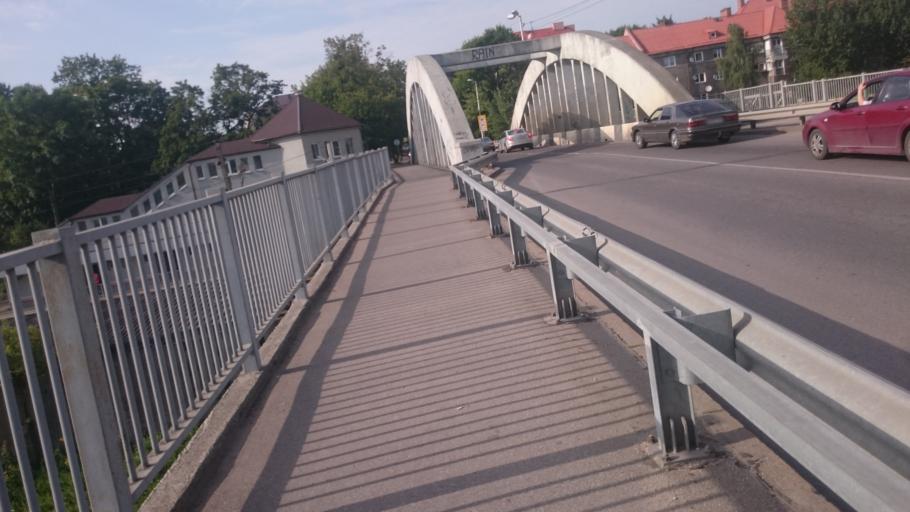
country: RU
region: Kaliningrad
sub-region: Gorod Kaliningrad
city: Kaliningrad
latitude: 54.7103
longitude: 20.4585
